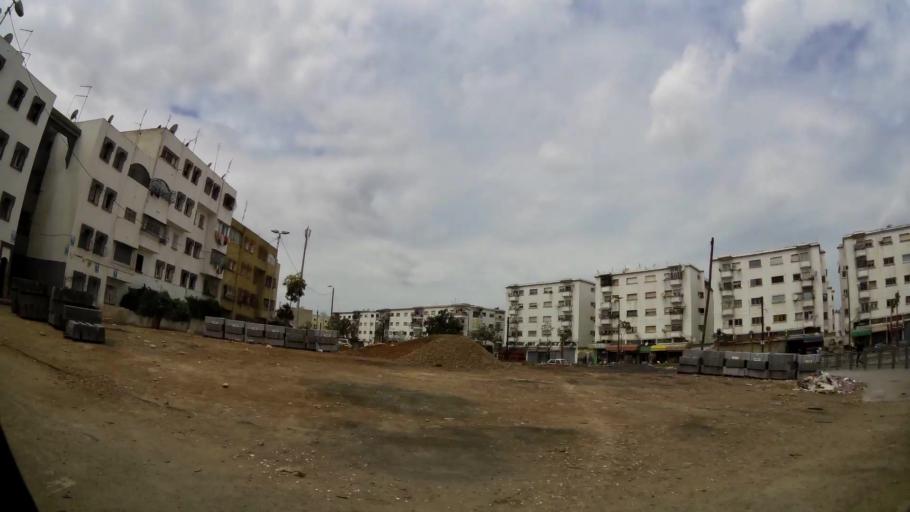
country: MA
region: Grand Casablanca
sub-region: Casablanca
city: Casablanca
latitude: 33.5937
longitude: -7.5540
